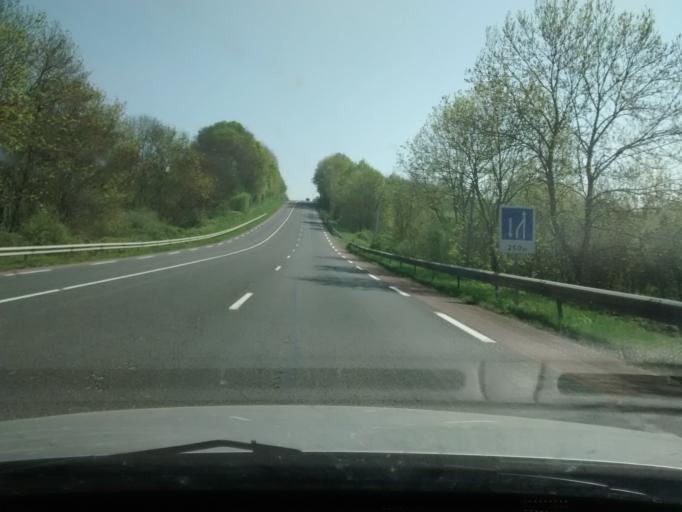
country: FR
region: Pays de la Loire
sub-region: Departement de la Sarthe
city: Loue
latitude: 48.0186
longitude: -0.1835
